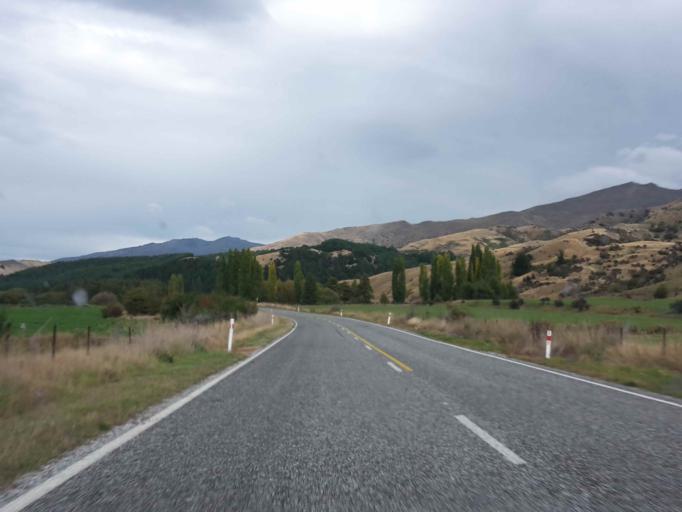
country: NZ
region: Otago
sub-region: Queenstown-Lakes District
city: Wanaka
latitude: -44.7553
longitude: 169.1081
